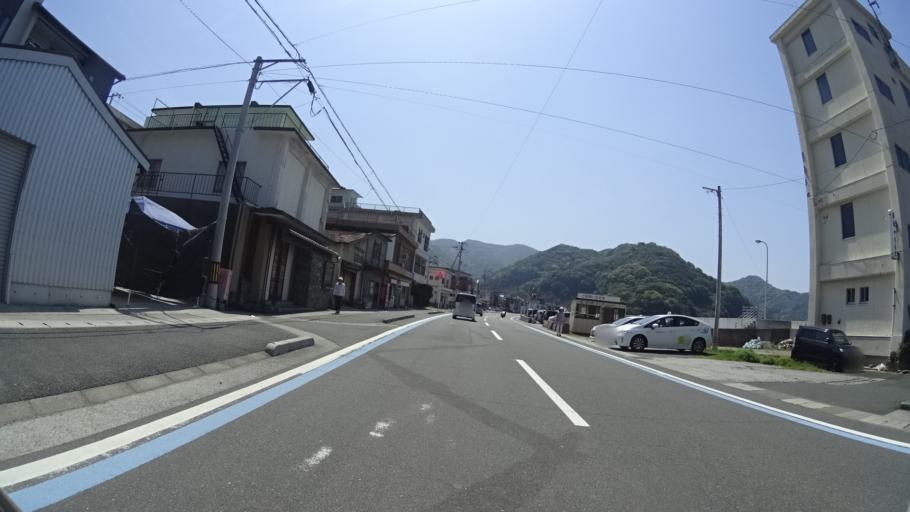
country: JP
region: Ehime
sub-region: Nishiuwa-gun
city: Ikata-cho
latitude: 33.3909
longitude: 132.1191
